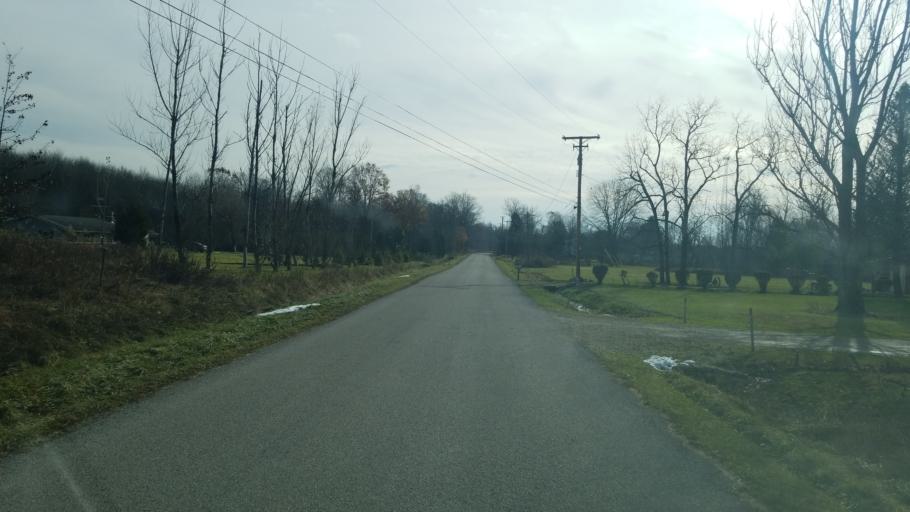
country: US
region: Ohio
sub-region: Ashtabula County
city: Roaming Shores
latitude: 41.6730
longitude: -80.9263
